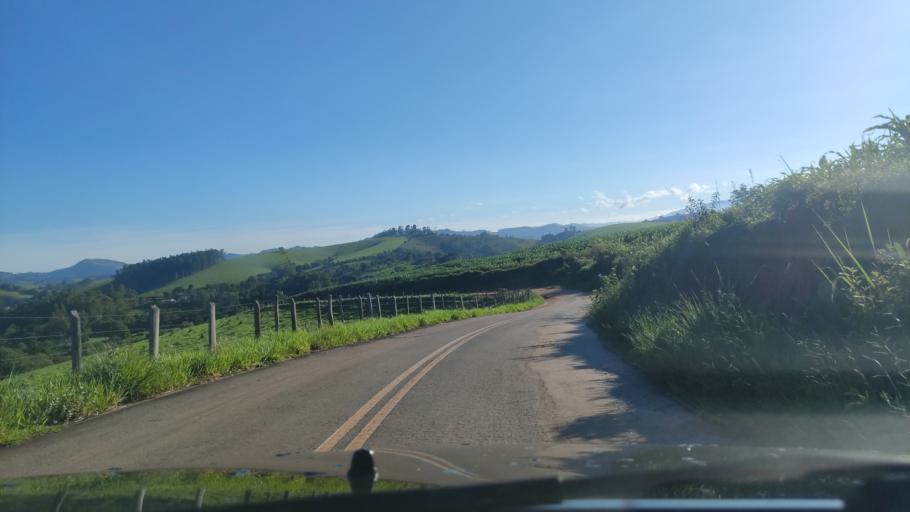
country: BR
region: Sao Paulo
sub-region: Aguas De Lindoia
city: Aguas de Lindoia
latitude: -22.5543
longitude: -46.6167
